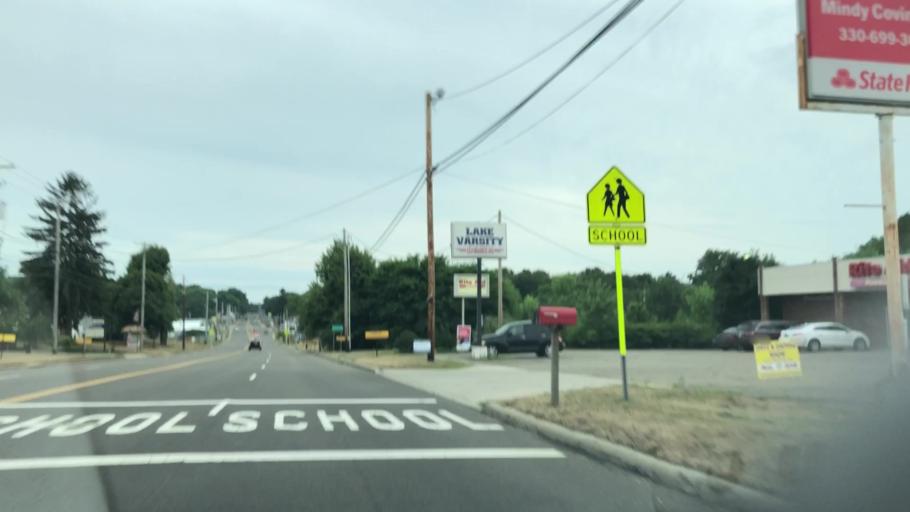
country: US
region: Ohio
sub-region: Stark County
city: Uniontown
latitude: 40.9808
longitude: -81.4068
